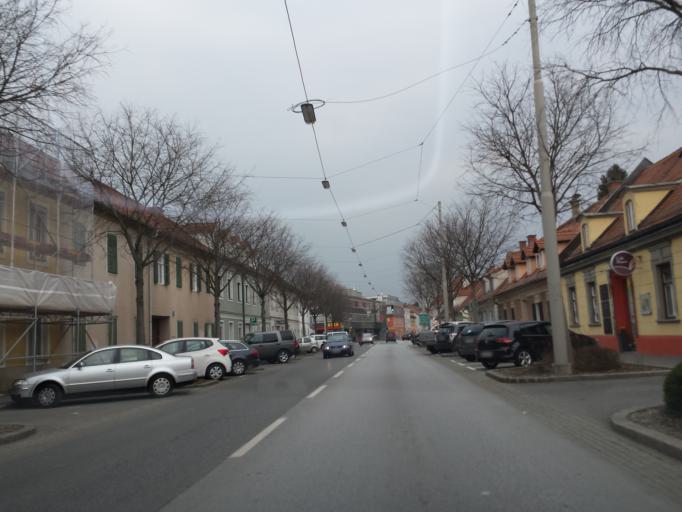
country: AT
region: Styria
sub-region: Graz Stadt
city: Graz
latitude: 47.0582
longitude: 15.4527
